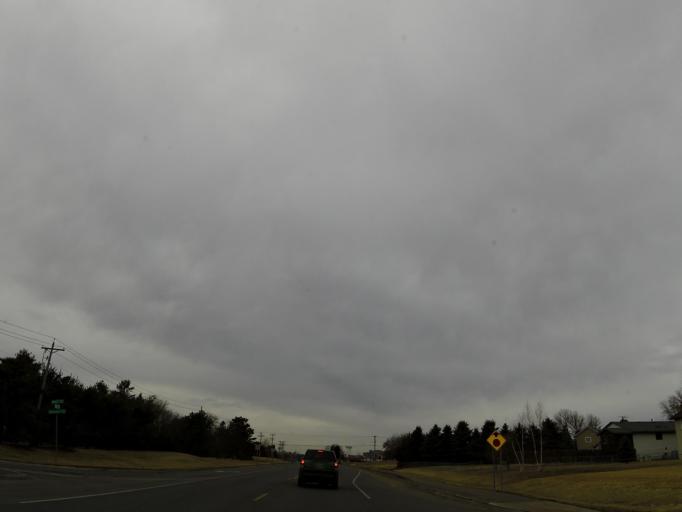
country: US
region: Minnesota
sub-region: Washington County
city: Cottage Grove
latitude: 44.8481
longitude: -92.9468
